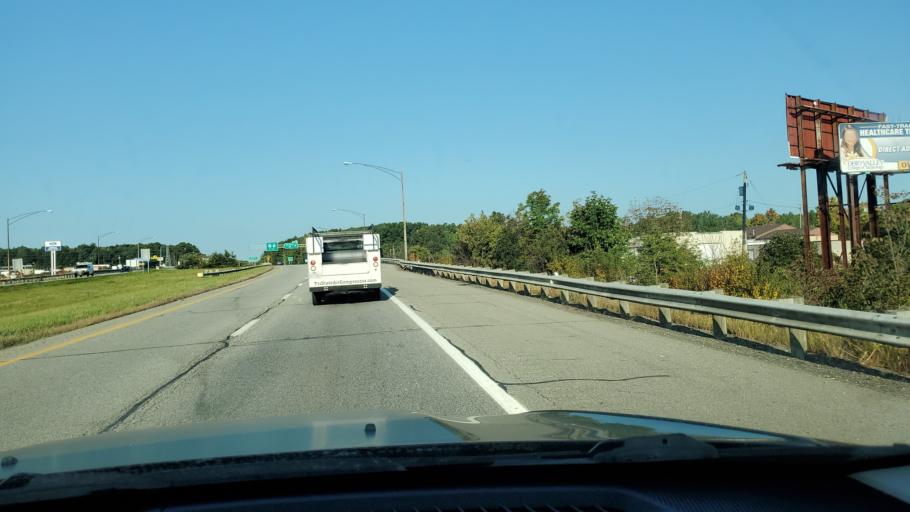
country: US
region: Ohio
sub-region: Trumbull County
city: Girard
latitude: 41.1227
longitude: -80.7088
